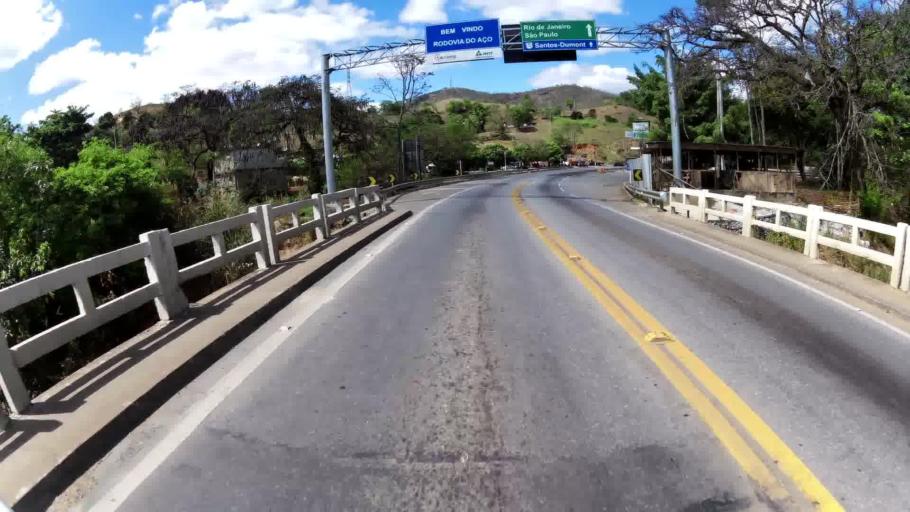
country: BR
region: Minas Gerais
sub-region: Alem Paraiba
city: Alem Paraiba
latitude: -21.8754
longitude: -42.6673
